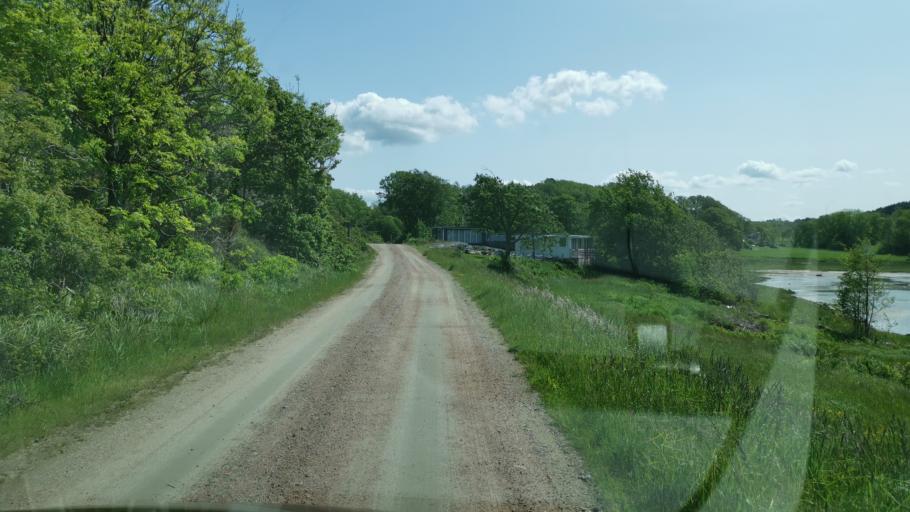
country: SE
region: Vaestra Goetaland
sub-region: Lysekils Kommun
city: Brastad
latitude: 58.2976
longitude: 11.5330
